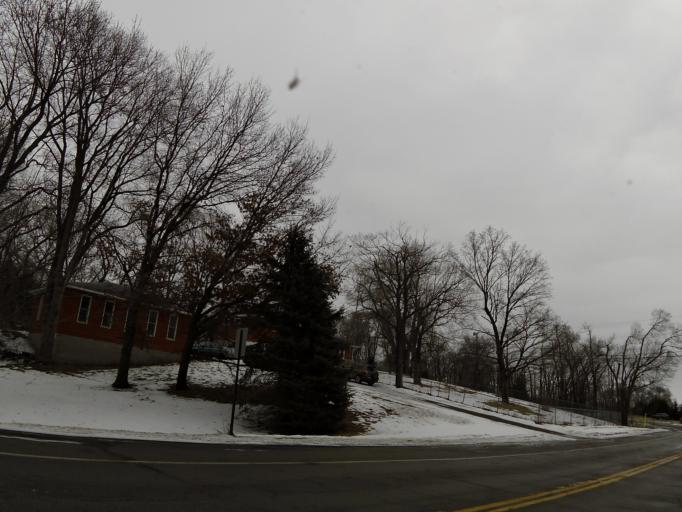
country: US
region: Minnesota
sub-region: Washington County
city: Cottage Grove
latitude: 44.7964
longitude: -92.8929
